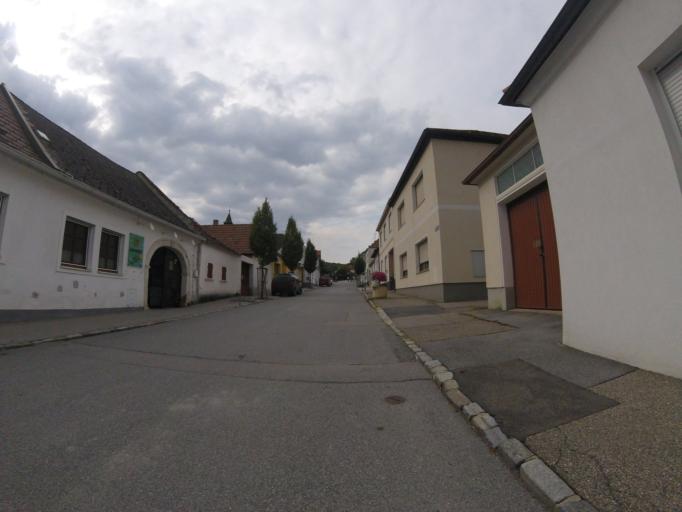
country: AT
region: Burgenland
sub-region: Eisenstadt-Umgebung
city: Donnerskirchen
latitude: 47.8974
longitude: 16.6431
